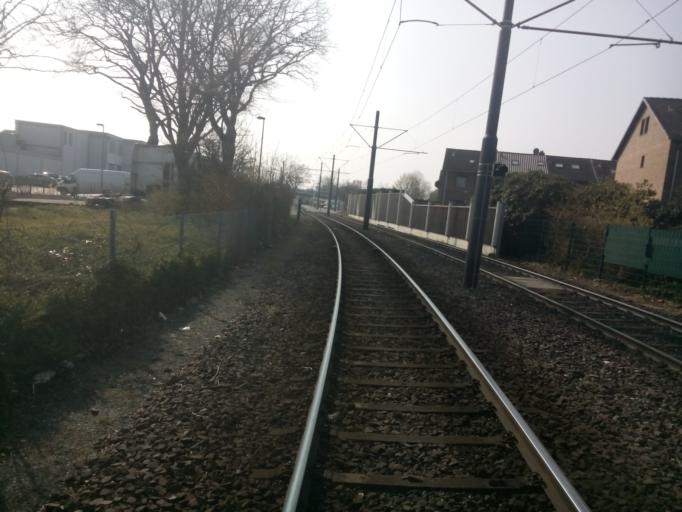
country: DE
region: Lower Saxony
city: Oyten
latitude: 53.0656
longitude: 8.9499
